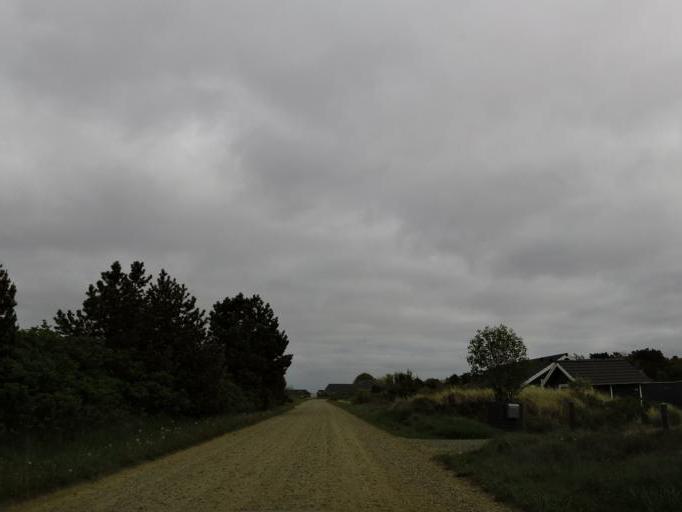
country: DE
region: Schleswig-Holstein
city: List
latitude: 55.1130
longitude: 8.5480
